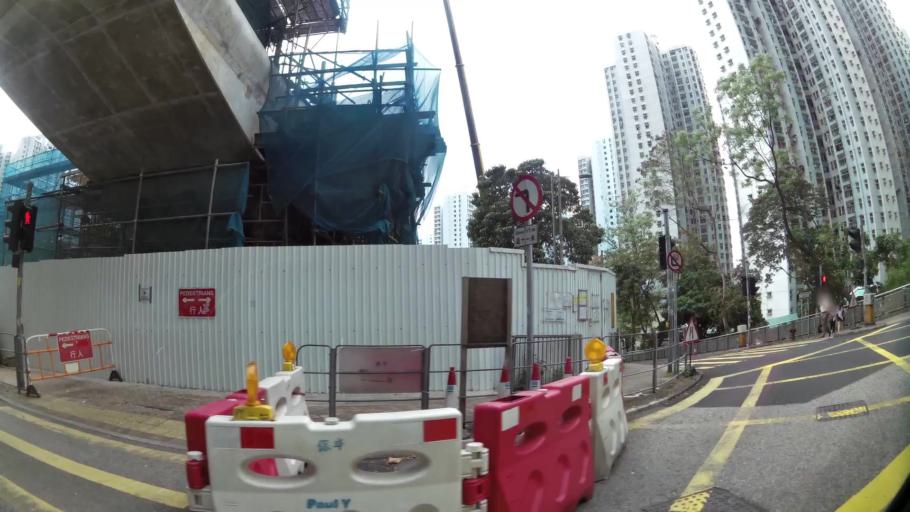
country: HK
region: Wong Tai Sin
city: Wong Tai Sin
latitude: 22.3504
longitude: 114.2004
